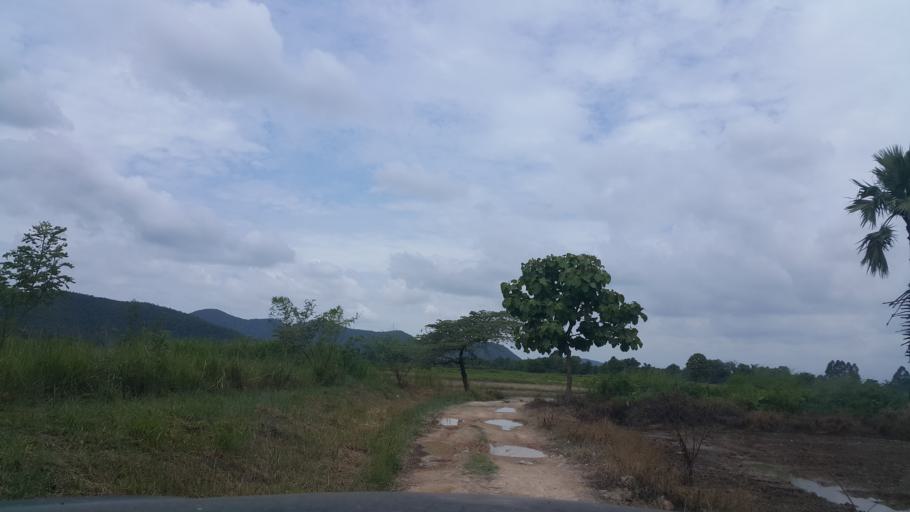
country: TH
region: Lamphun
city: Ban Thi
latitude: 18.6408
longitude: 99.1480
